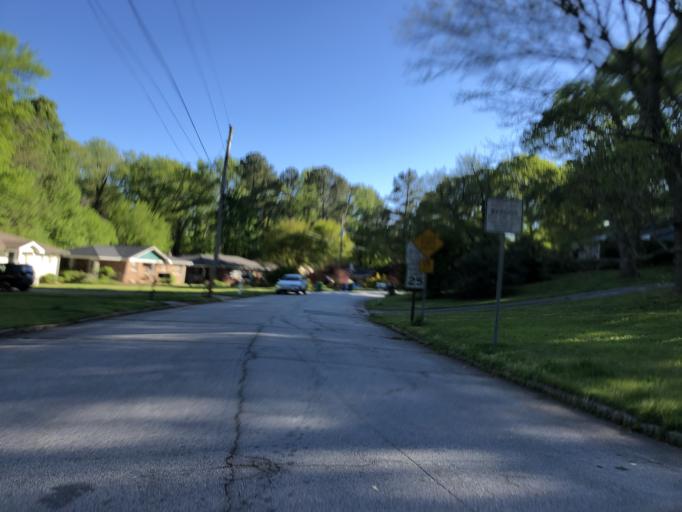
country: US
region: Georgia
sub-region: DeKalb County
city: North Decatur
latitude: 33.8080
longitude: -84.2880
